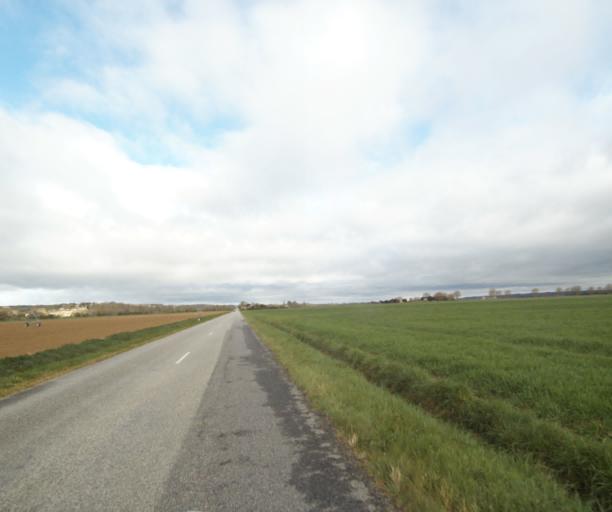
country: FR
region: Midi-Pyrenees
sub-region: Departement de l'Ariege
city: Saverdun
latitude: 43.2522
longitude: 1.5476
